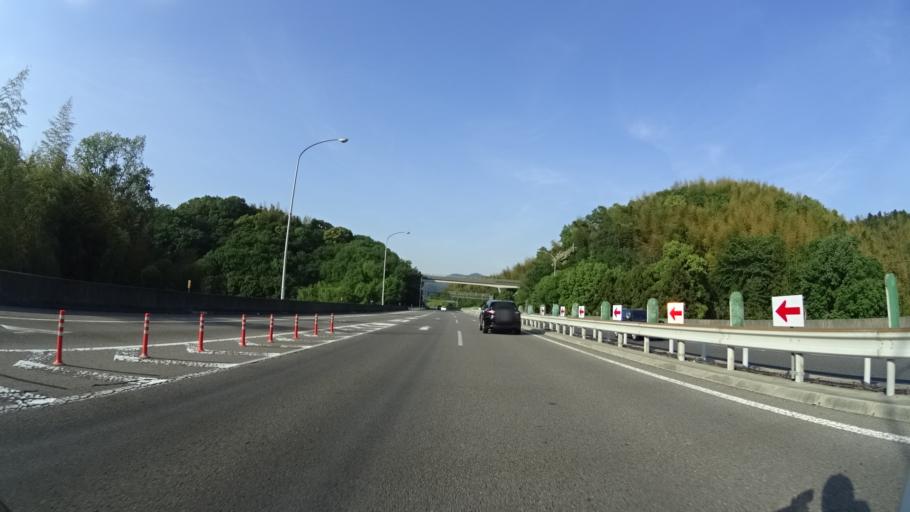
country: JP
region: Ehime
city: Kawanoecho
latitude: 33.9848
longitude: 133.5882
